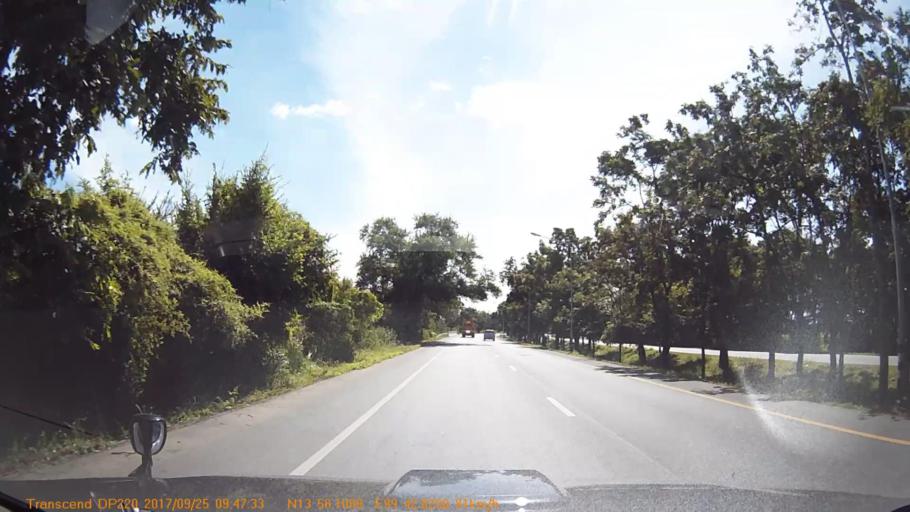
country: TH
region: Kanchanaburi
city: Tha Maka
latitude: 13.9684
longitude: 99.7143
